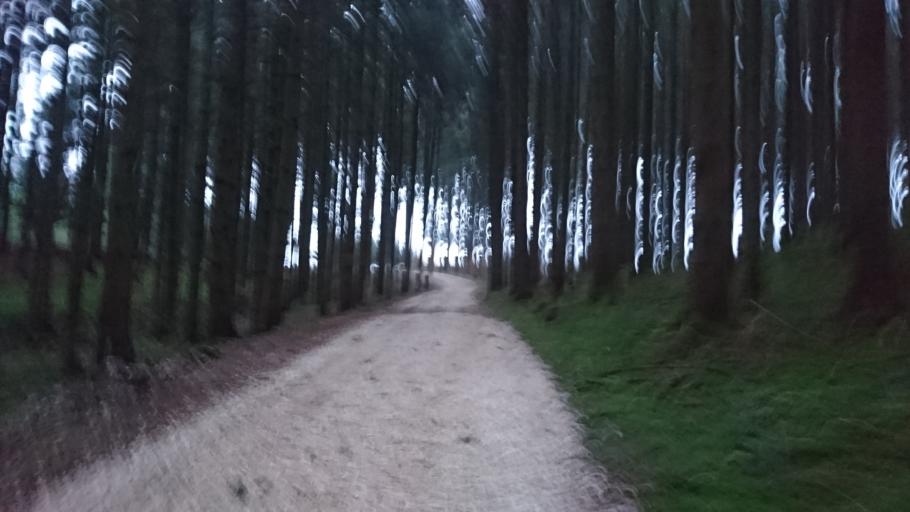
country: DE
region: Bavaria
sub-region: Swabia
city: Altenmunster
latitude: 48.4365
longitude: 10.6126
